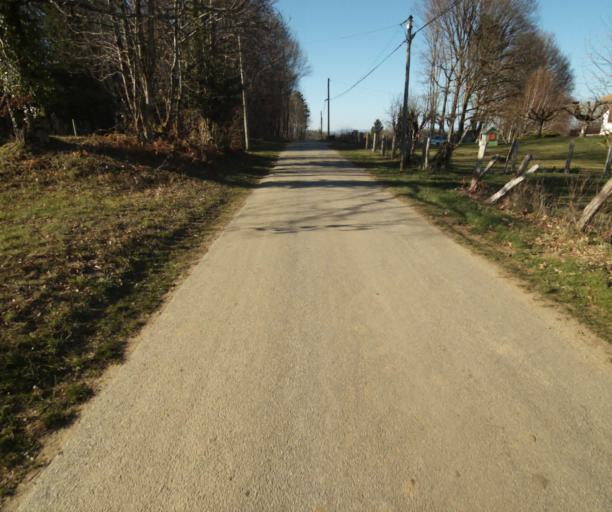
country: FR
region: Limousin
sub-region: Departement de la Correze
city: Seilhac
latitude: 45.3915
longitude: 1.7065
